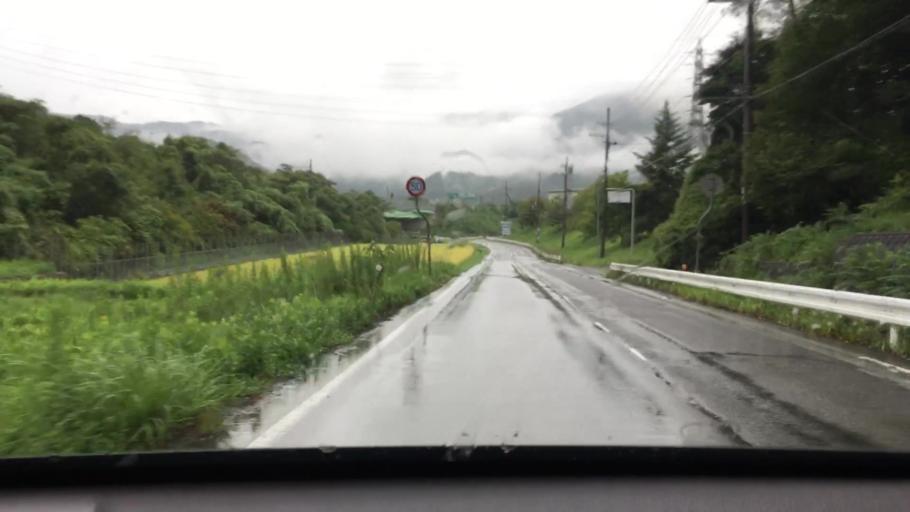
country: JP
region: Hyogo
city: Toyooka
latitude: 35.3116
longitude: 134.8545
